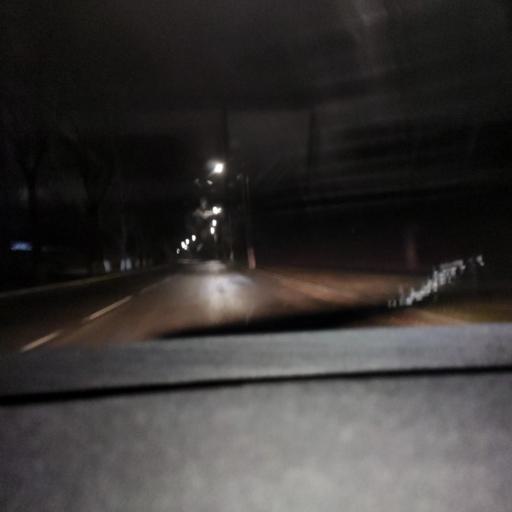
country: RU
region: Voronezj
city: Semiluki
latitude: 51.6897
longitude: 39.0377
